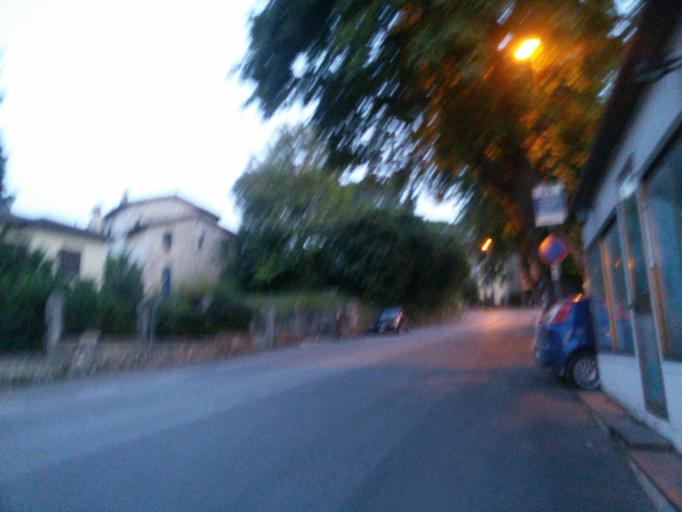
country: IT
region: Umbria
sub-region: Provincia di Perugia
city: Spoleto
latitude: 42.7334
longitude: 12.7306
